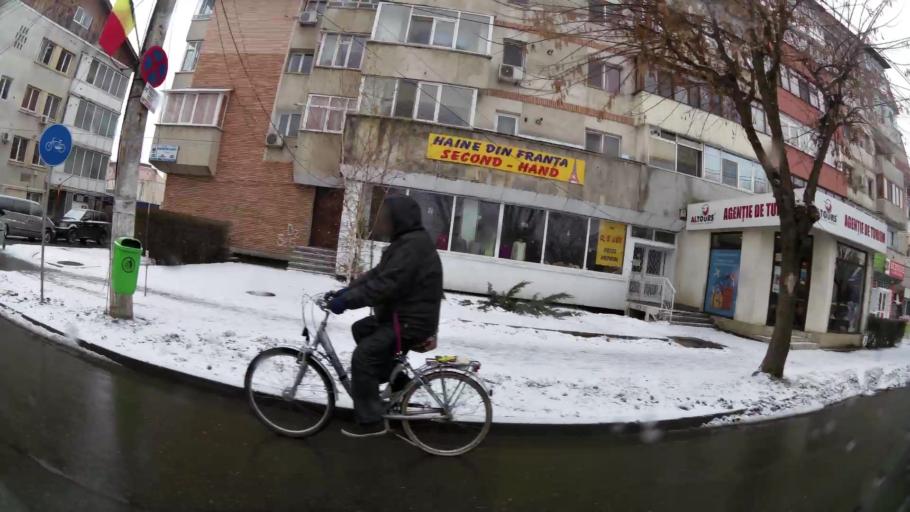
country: RO
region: Dambovita
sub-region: Municipiul Targoviste
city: Targoviste
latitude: 44.9175
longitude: 25.4679
